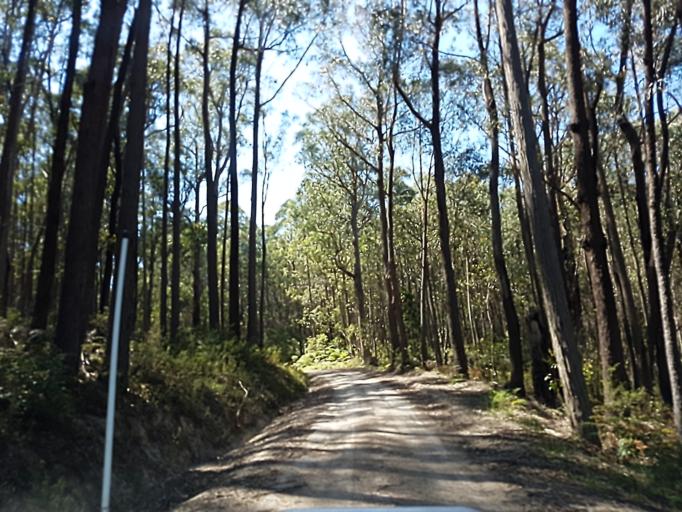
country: AU
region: Victoria
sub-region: East Gippsland
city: Lakes Entrance
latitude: -37.2888
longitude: 148.3102
